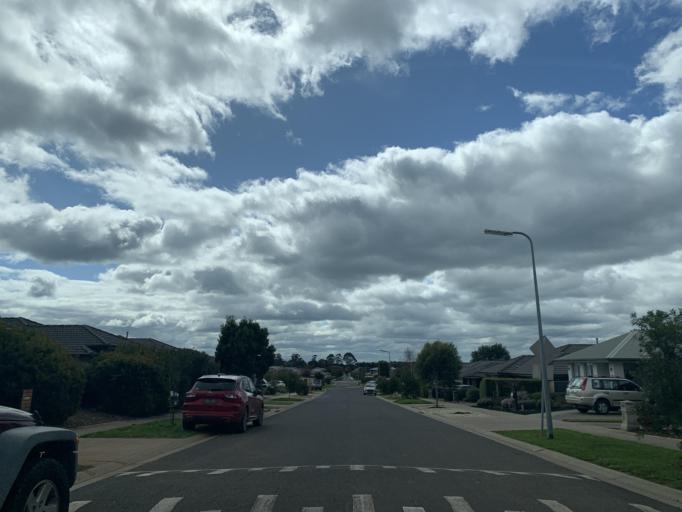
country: AU
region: Victoria
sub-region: Whittlesea
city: Whittlesea
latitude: -37.2925
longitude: 144.9354
